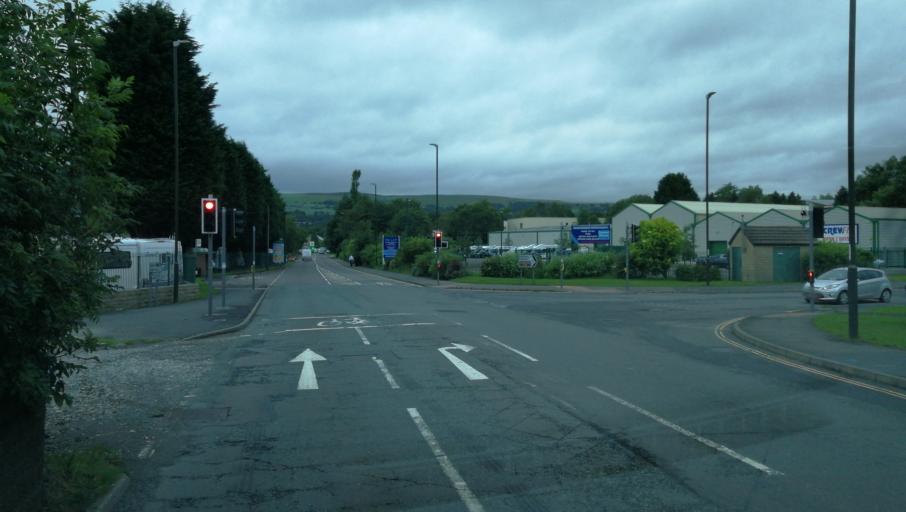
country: GB
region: England
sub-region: Borough of Tameside
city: Longdendale
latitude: 53.4510
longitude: -1.9800
